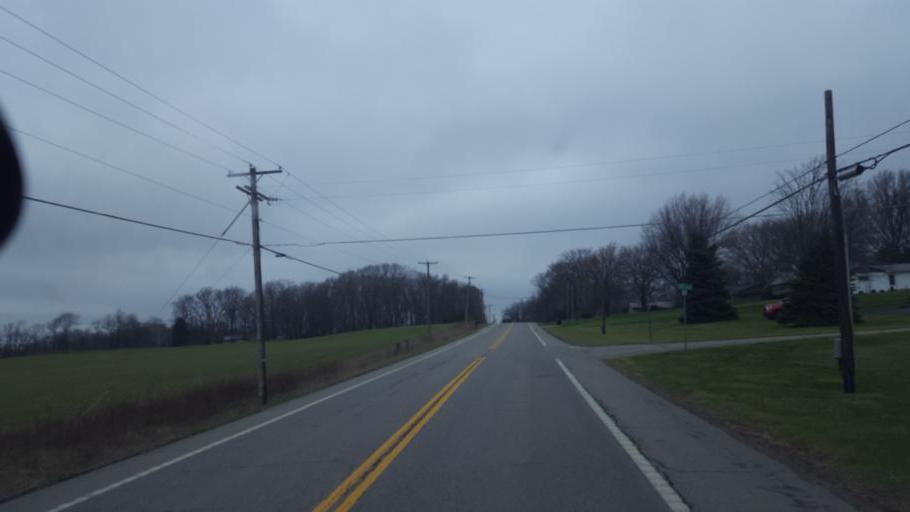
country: US
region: Ohio
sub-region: Ashland County
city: Ashland
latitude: 40.8109
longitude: -82.2744
